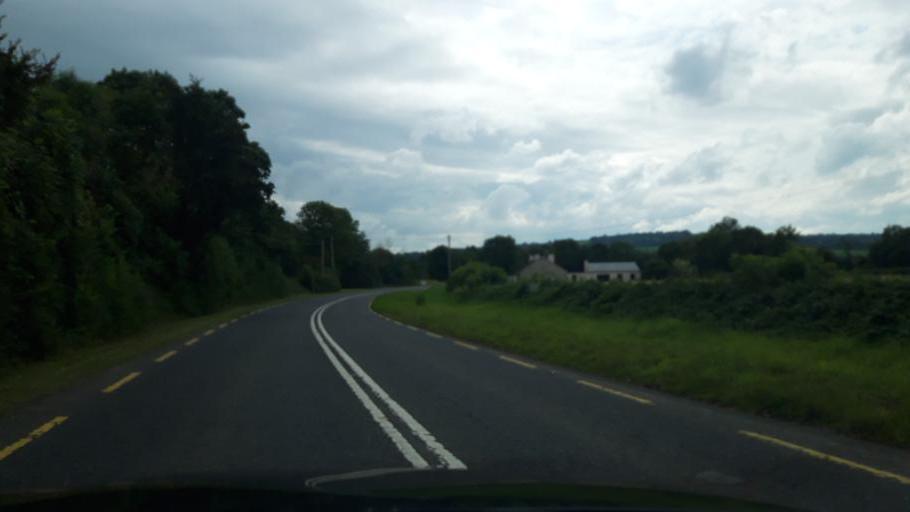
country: IE
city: Ballylinan
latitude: 52.9320
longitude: -7.0547
